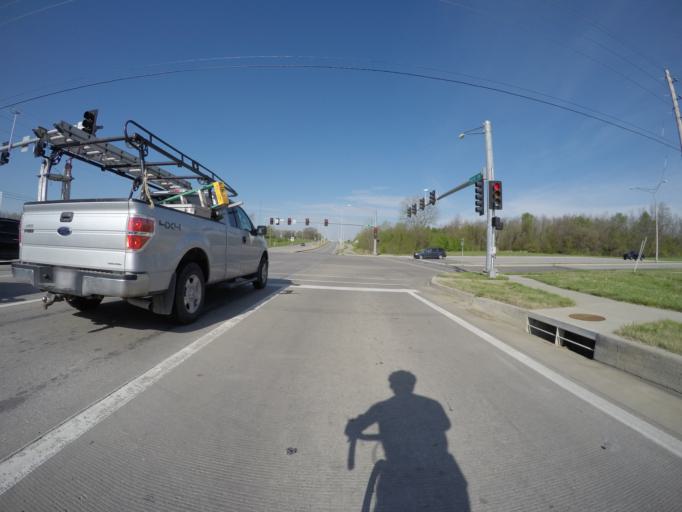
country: US
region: Missouri
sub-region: Cass County
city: Lake Winnebago
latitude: 38.8534
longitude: -94.3983
